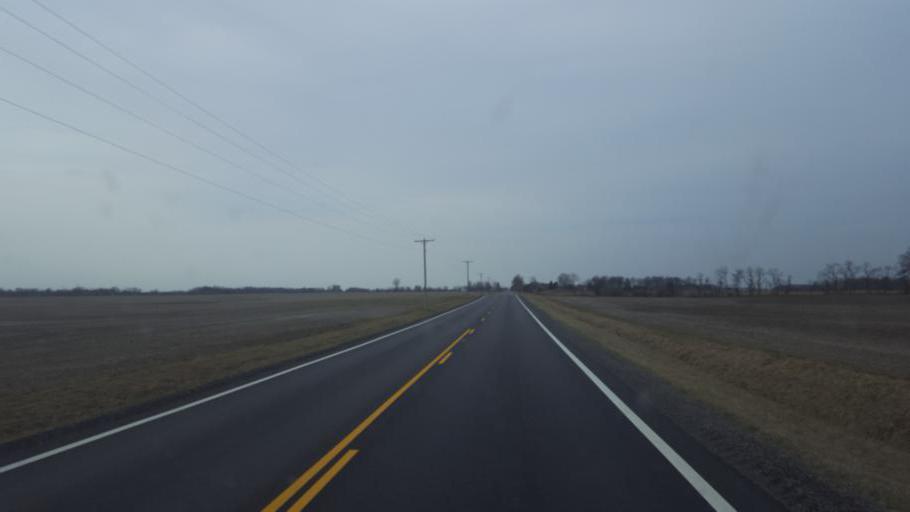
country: US
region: Ohio
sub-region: Marion County
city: Marion
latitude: 40.6688
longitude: -83.0143
